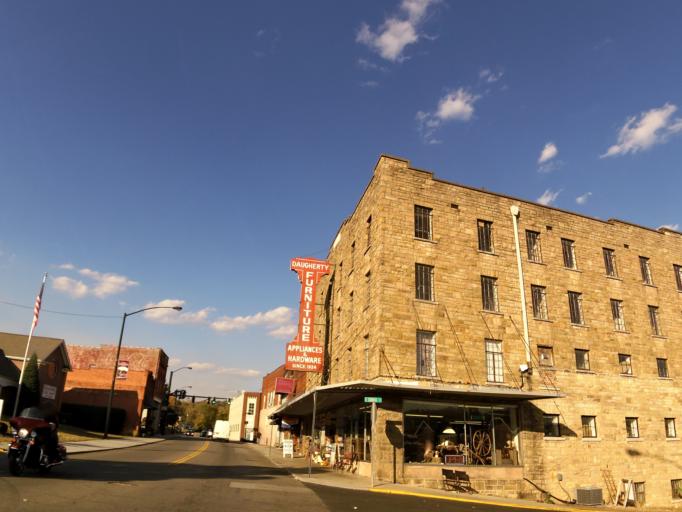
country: US
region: Tennessee
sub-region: Anderson County
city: Clinton
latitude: 36.1024
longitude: -84.1324
